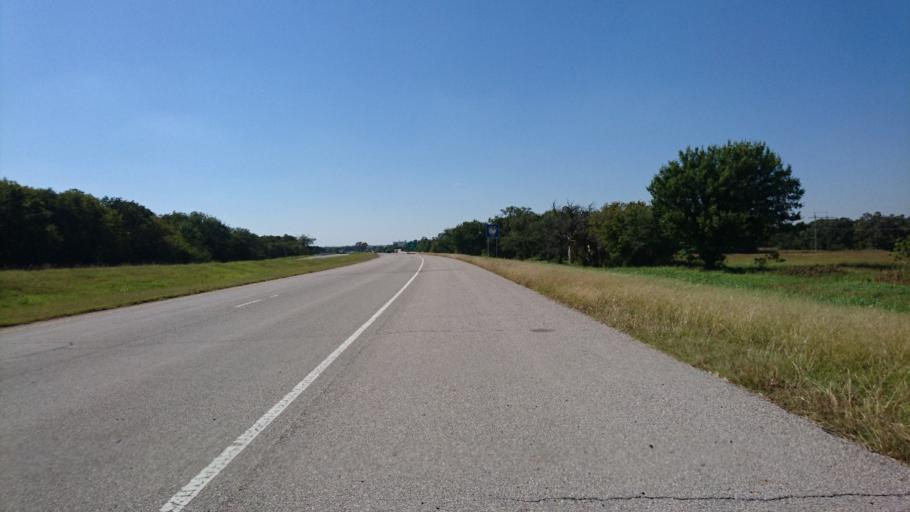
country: US
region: Oklahoma
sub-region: Custer County
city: Clinton
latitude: 35.5159
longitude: -98.9276
